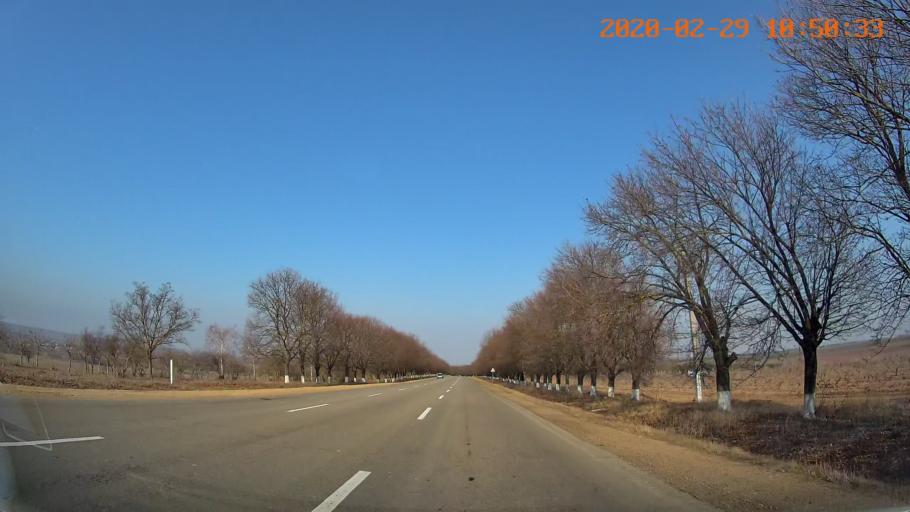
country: MD
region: Telenesti
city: Grigoriopol
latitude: 47.0844
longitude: 29.3740
